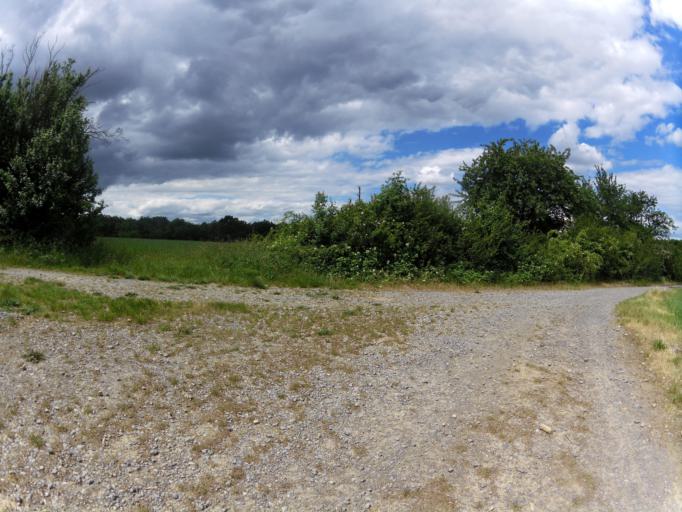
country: DE
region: Bavaria
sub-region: Regierungsbezirk Unterfranken
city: Thungersheim
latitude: 49.8811
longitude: 9.8771
